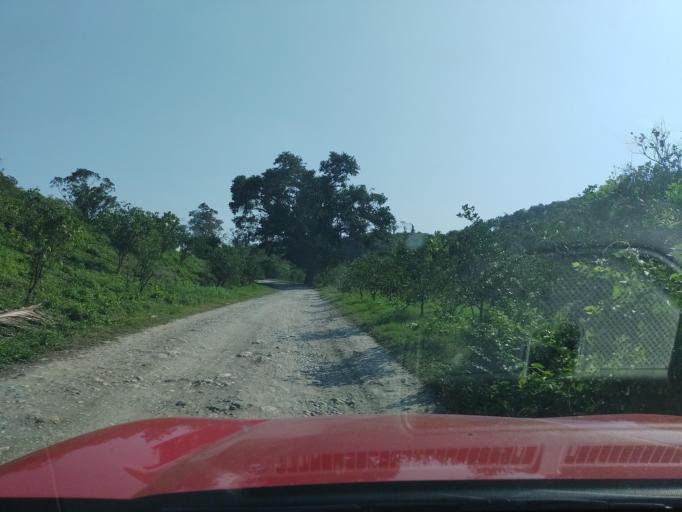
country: MX
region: Veracruz
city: Agua Dulce
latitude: 20.3478
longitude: -97.1772
